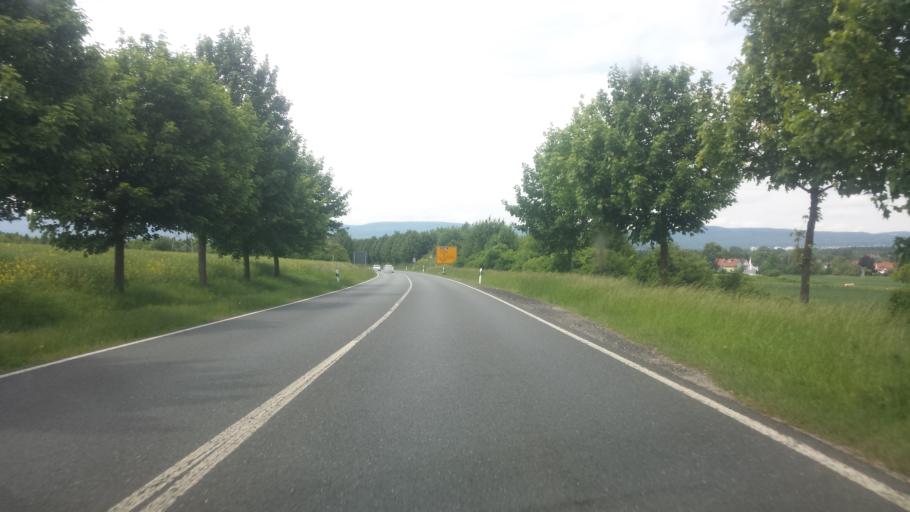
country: DE
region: Hesse
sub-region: Regierungsbezirk Darmstadt
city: Friedrichsdorf
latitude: 50.2183
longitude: 8.6874
